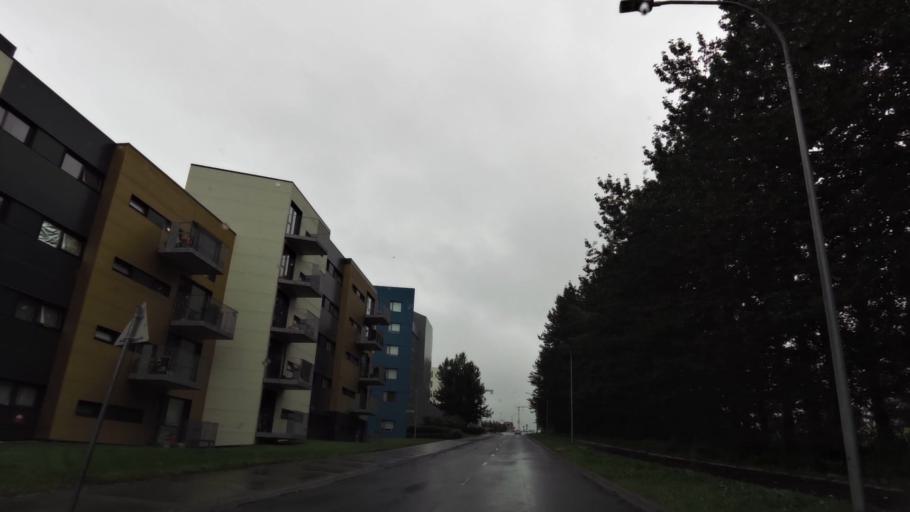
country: IS
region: Capital Region
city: Reykjavik
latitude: 64.1215
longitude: -21.8933
